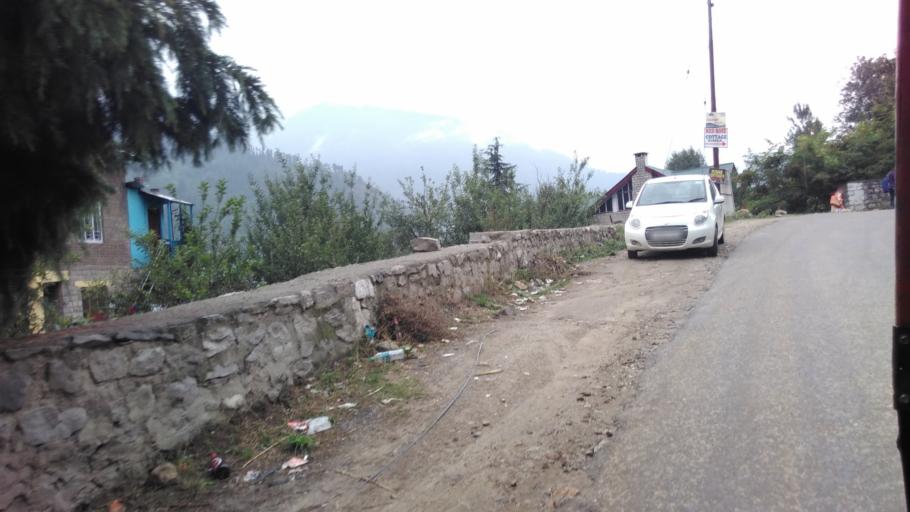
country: IN
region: Himachal Pradesh
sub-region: Kulu
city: Manali
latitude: 32.2211
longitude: 77.1890
